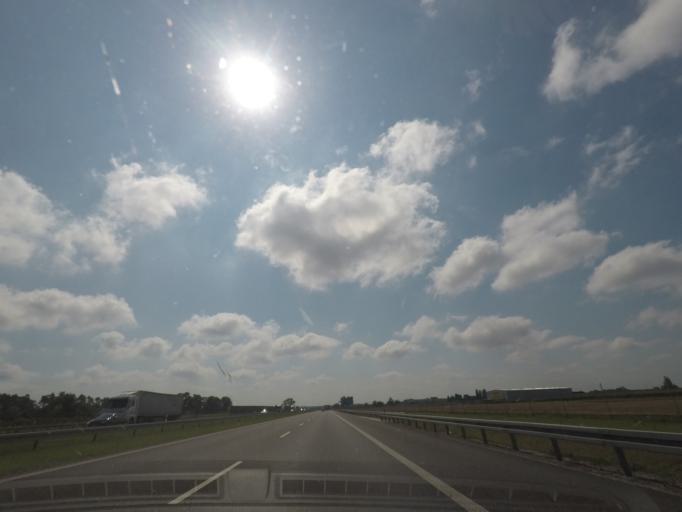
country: PL
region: Kujawsko-Pomorskie
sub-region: Powiat wloclawski
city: Brzesc Kujawski
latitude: 52.6350
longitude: 18.9536
